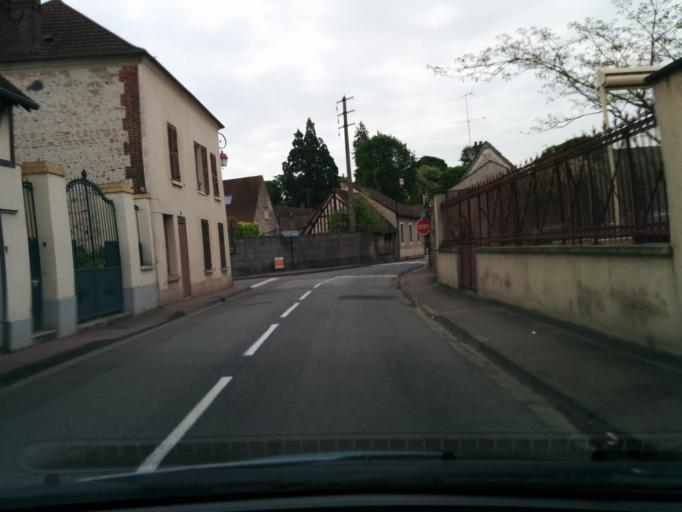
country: FR
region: Haute-Normandie
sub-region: Departement de l'Eure
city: Gasny
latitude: 49.0893
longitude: 1.6069
